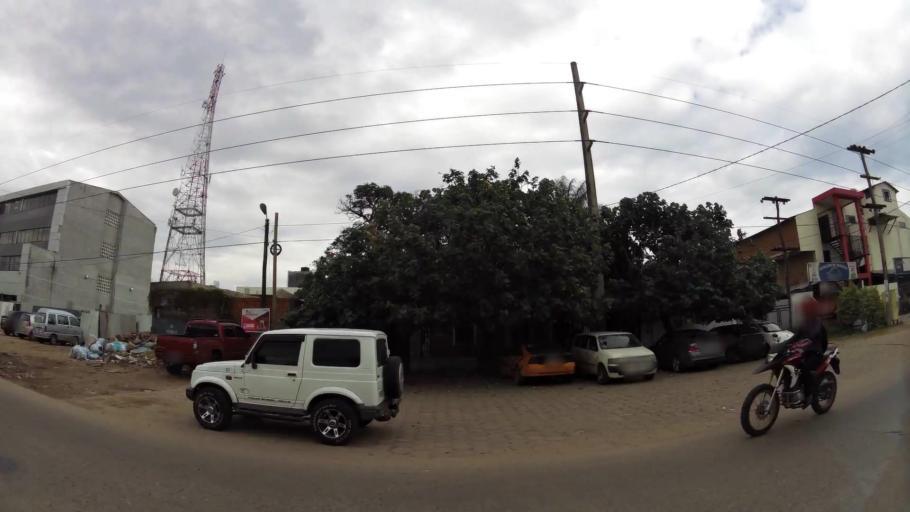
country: BO
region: Santa Cruz
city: Santa Cruz de la Sierra
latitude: -17.7601
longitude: -63.1775
